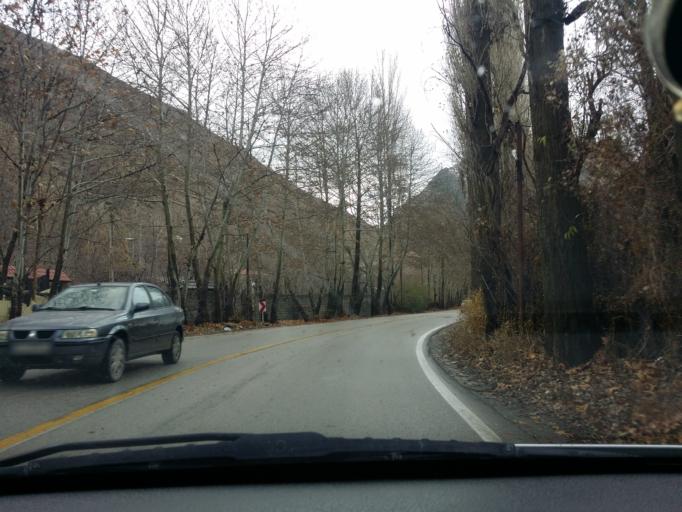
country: IR
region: Tehran
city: Tajrish
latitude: 36.0281
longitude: 51.2426
